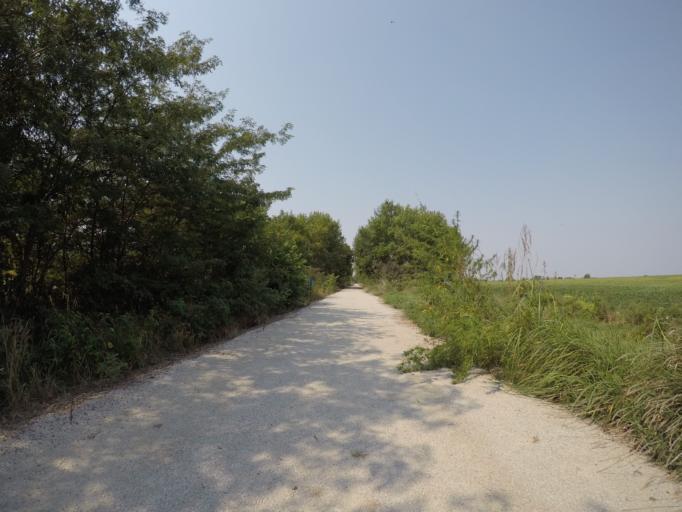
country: US
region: Nebraska
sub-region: Gage County
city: Beatrice
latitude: 40.2529
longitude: -96.7113
